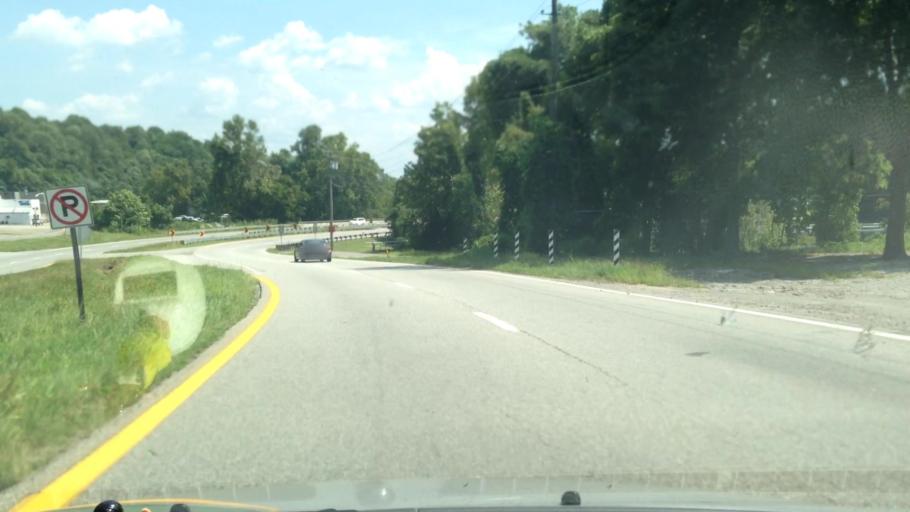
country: US
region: Virginia
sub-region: City of Martinsville
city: Martinsville
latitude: 36.6662
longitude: -79.8837
